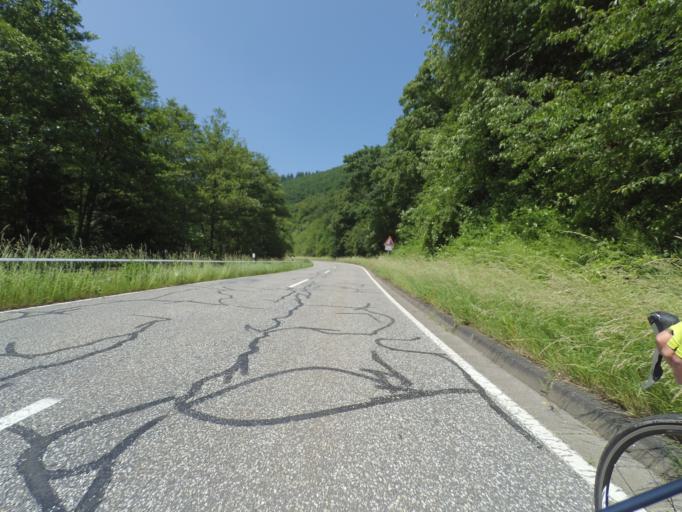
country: DE
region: Rheinland-Pfalz
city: Sankt Goar
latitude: 50.1475
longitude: 7.6873
